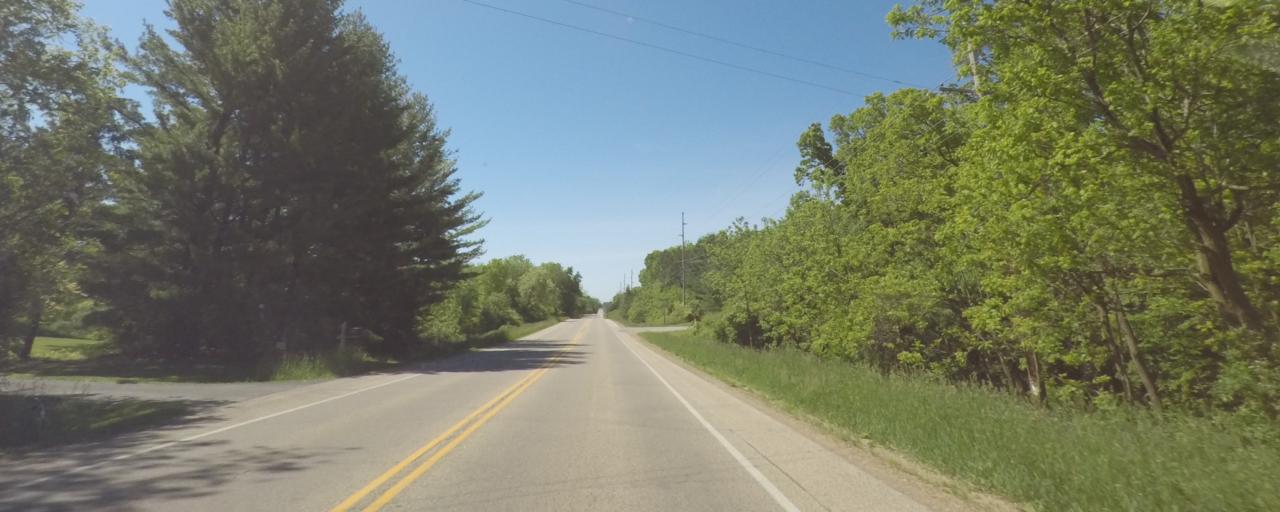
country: US
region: Wisconsin
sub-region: Green County
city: Brooklyn
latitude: 42.8771
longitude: -89.3691
